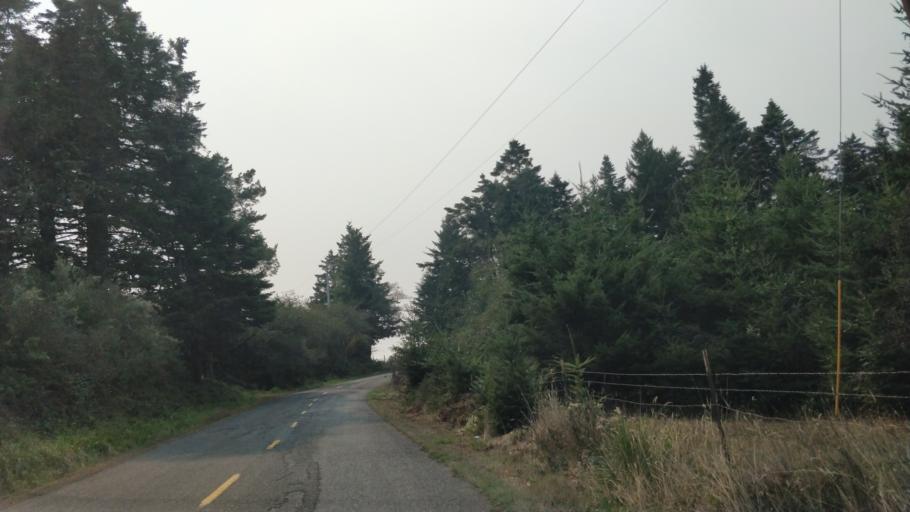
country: US
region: California
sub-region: Humboldt County
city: Ferndale
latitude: 40.4539
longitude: -124.3756
